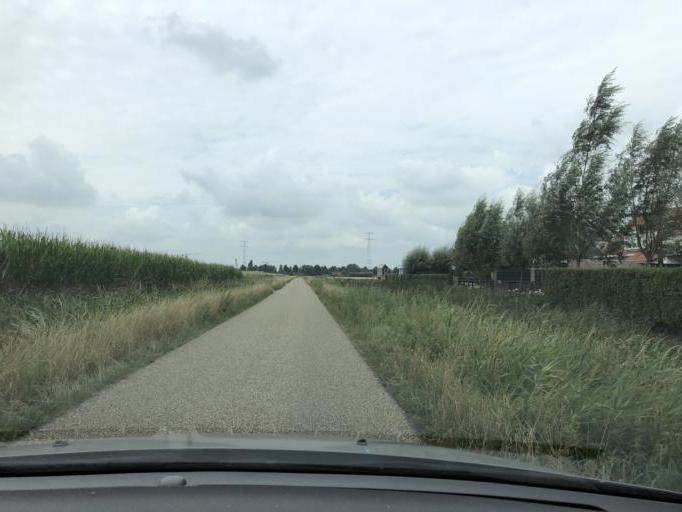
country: NL
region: Zeeland
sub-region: Gemeente Reimerswaal
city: Yerseke
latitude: 51.4512
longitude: 4.0244
